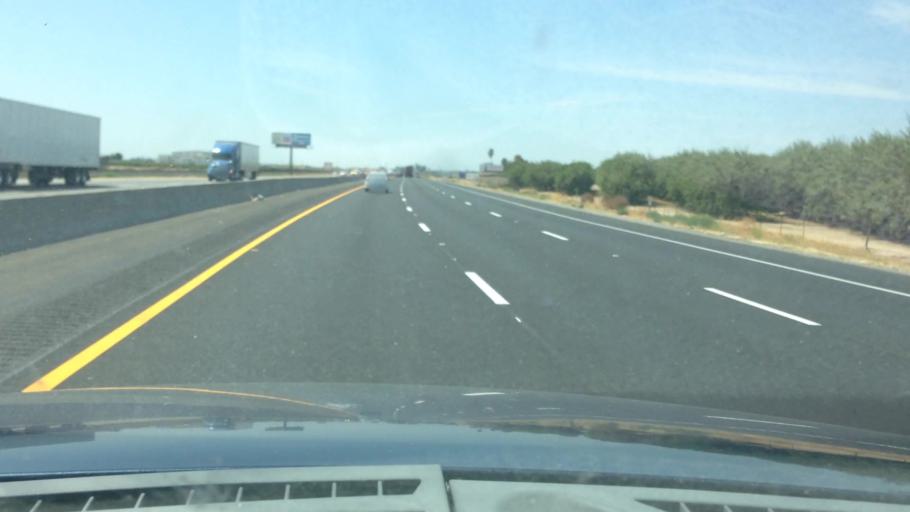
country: US
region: California
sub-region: Kern County
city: McFarland
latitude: 35.7130
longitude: -119.2356
